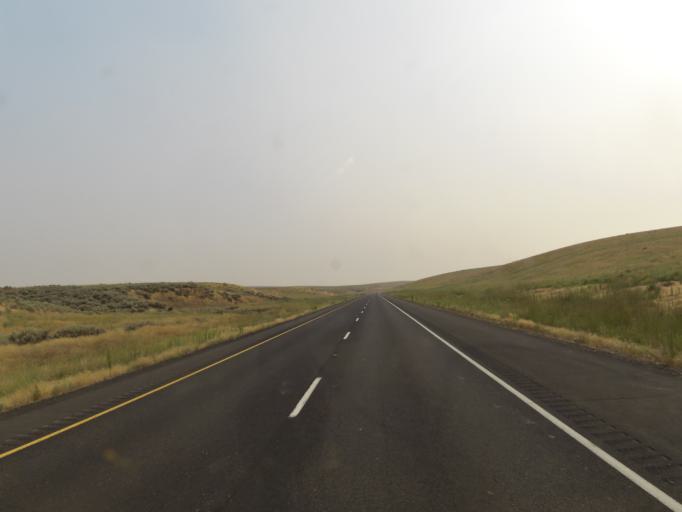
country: US
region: Washington
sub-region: Adams County
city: Ritzville
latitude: 46.8987
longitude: -118.6145
